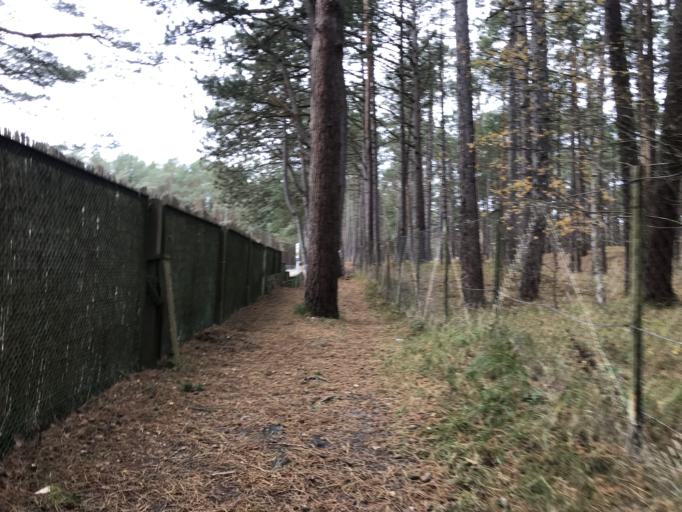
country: PL
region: Pomeranian Voivodeship
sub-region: Powiat leborski
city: Leba
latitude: 54.7635
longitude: 17.5356
